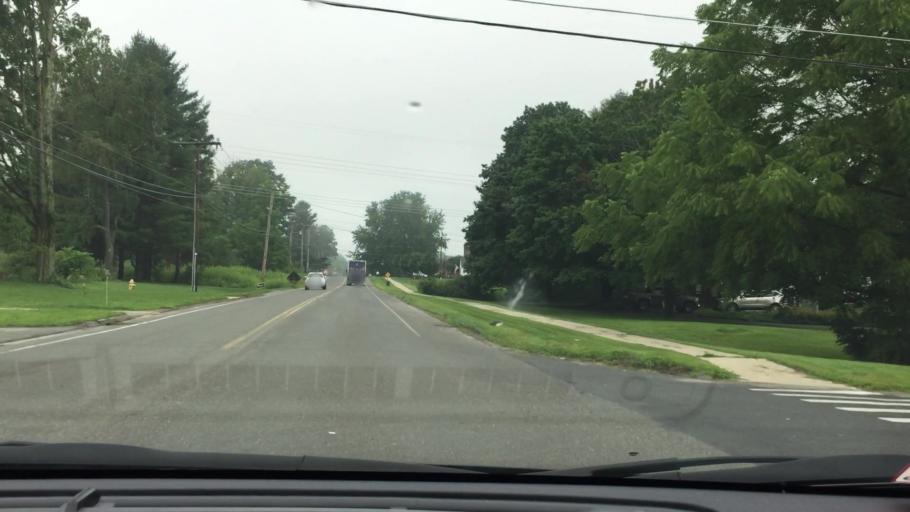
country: US
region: Massachusetts
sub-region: Berkshire County
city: Pittsfield
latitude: 42.4312
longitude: -73.2061
